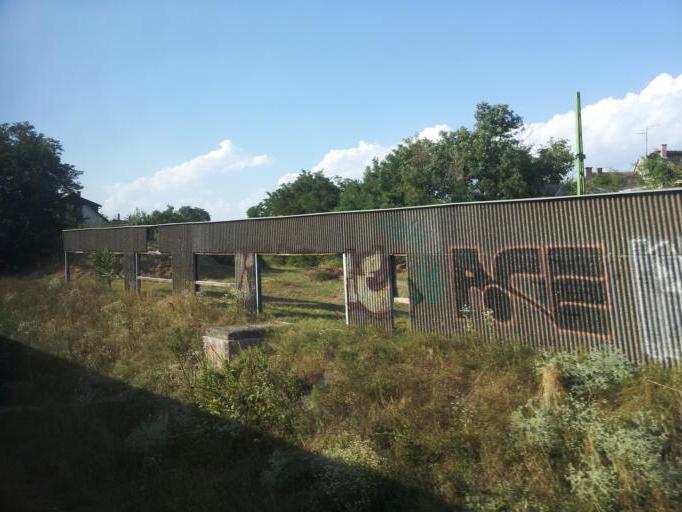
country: HU
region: Budapest
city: Budapest XXIII. keruelet
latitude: 47.4121
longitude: 19.1161
